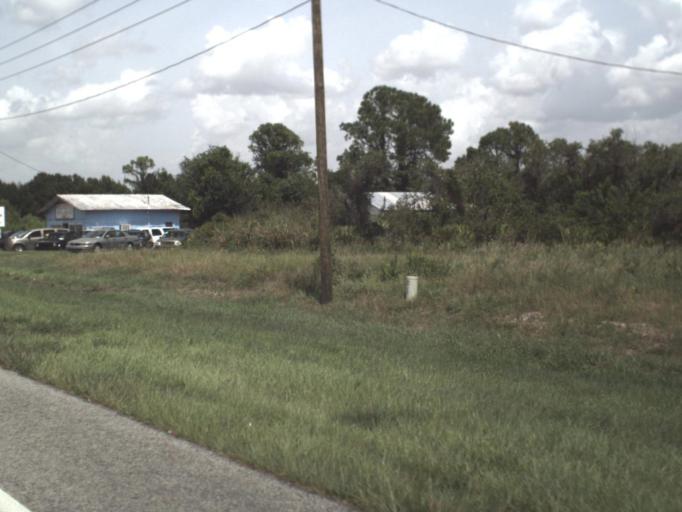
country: US
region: Florida
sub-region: Highlands County
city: Avon Park
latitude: 27.5354
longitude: -81.5024
